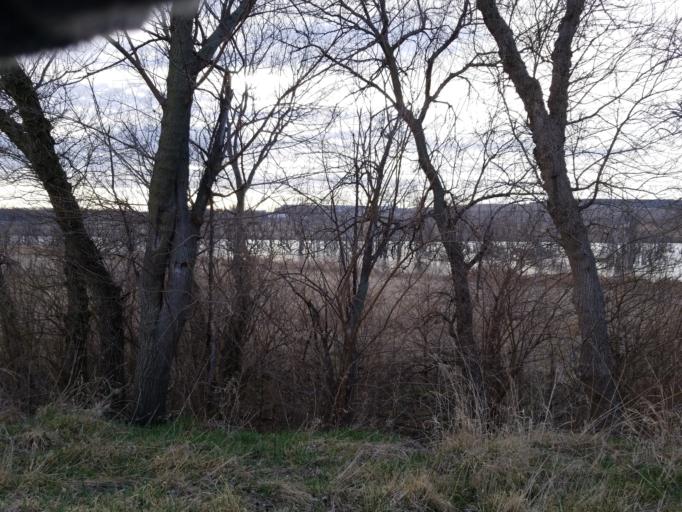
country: US
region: Nebraska
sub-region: Sarpy County
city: Chalco
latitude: 41.1511
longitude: -96.1140
